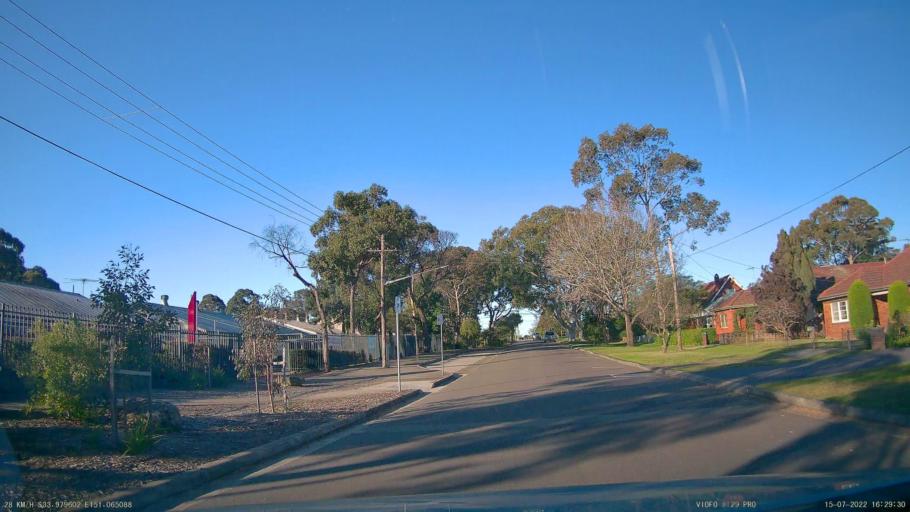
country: AU
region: New South Wales
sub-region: Hurstville
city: Oatley
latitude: -33.9796
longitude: 151.0653
